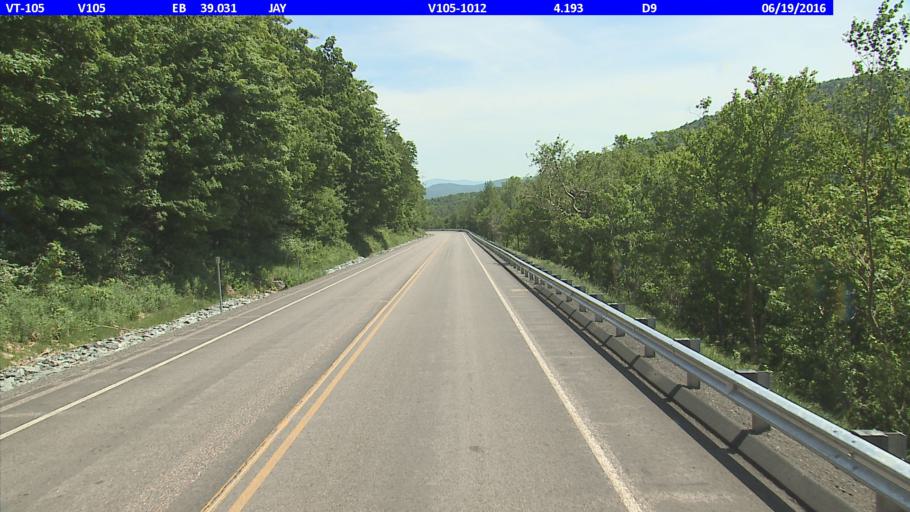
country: CA
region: Quebec
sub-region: Monteregie
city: Sutton
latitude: 44.9882
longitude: -72.4970
